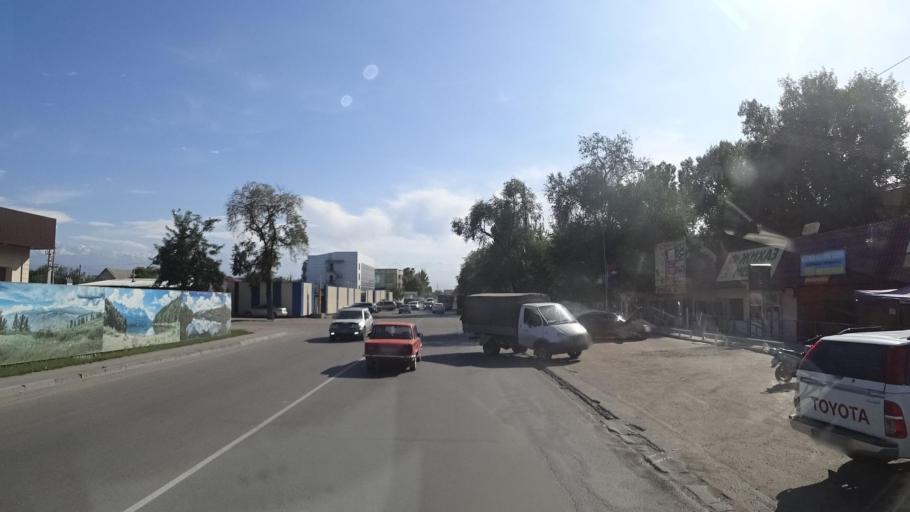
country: KZ
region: Almaty Oblysy
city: Energeticheskiy
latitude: 43.4192
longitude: 77.0221
